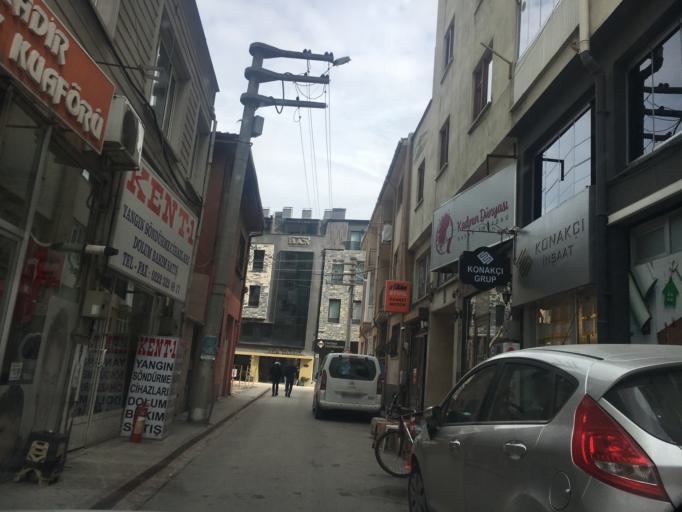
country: TR
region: Eskisehir
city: Eskisehir
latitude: 39.7796
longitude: 30.5157
